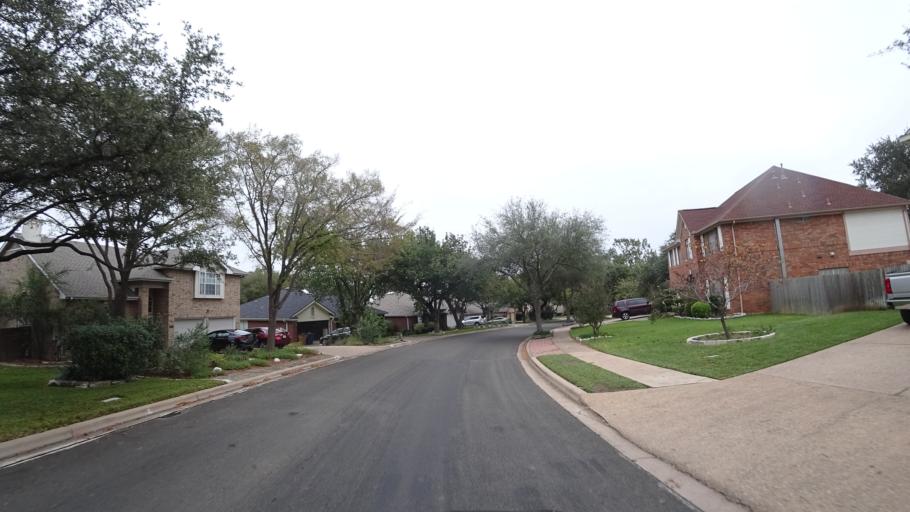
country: US
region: Texas
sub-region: Travis County
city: Shady Hollow
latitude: 30.1879
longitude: -97.8910
